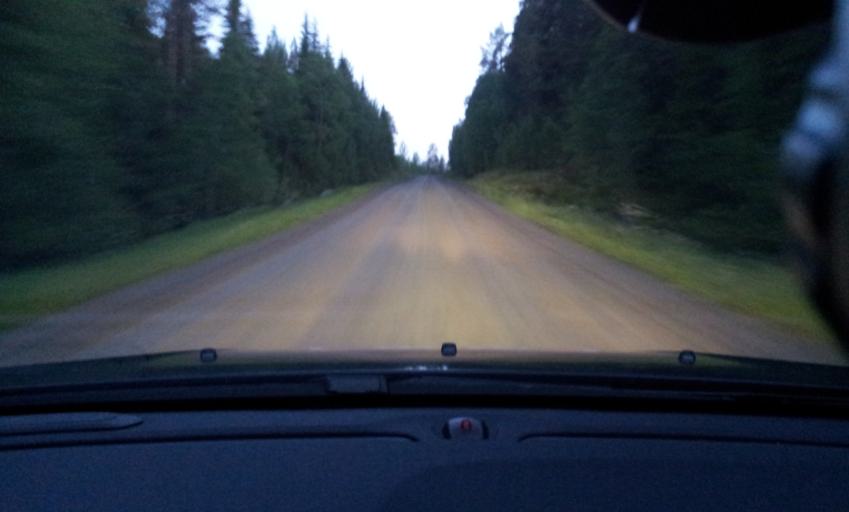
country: SE
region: Vaesternorrland
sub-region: Ange Kommun
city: Ange
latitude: 62.7204
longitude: 15.6343
